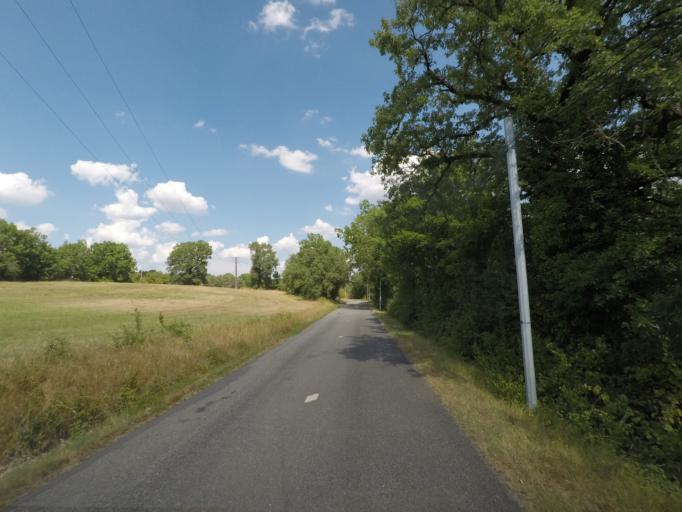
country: FR
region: Midi-Pyrenees
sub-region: Departement du Lot
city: Le Vigan
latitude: 44.6031
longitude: 1.5863
